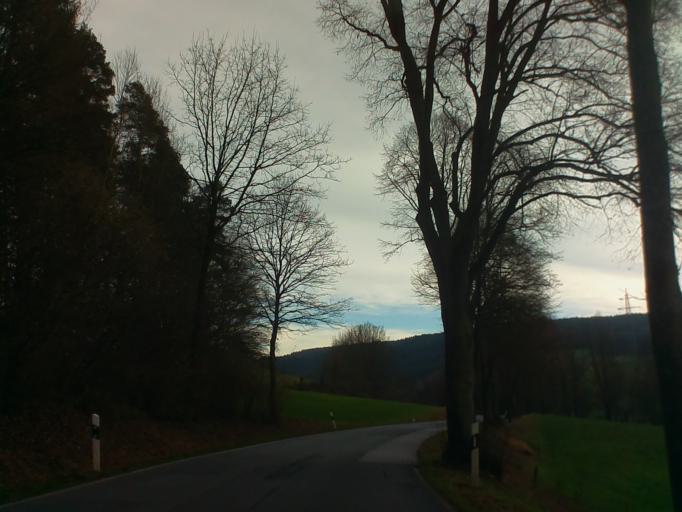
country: DE
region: Hesse
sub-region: Regierungsbezirk Darmstadt
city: Erbach
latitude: 49.6271
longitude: 8.9422
